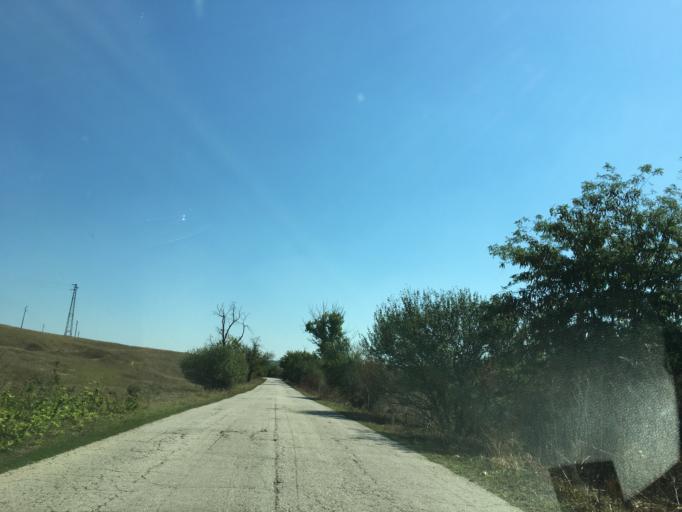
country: BG
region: Pleven
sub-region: Obshtina Knezha
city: Knezha
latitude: 43.5394
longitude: 24.1079
